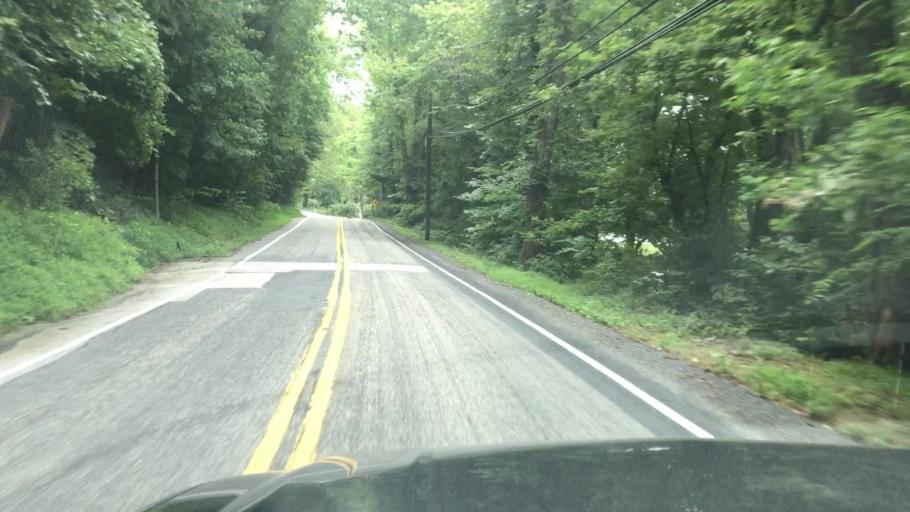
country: US
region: Pennsylvania
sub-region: Cumberland County
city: Shiremanstown
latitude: 40.2604
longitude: -76.9767
